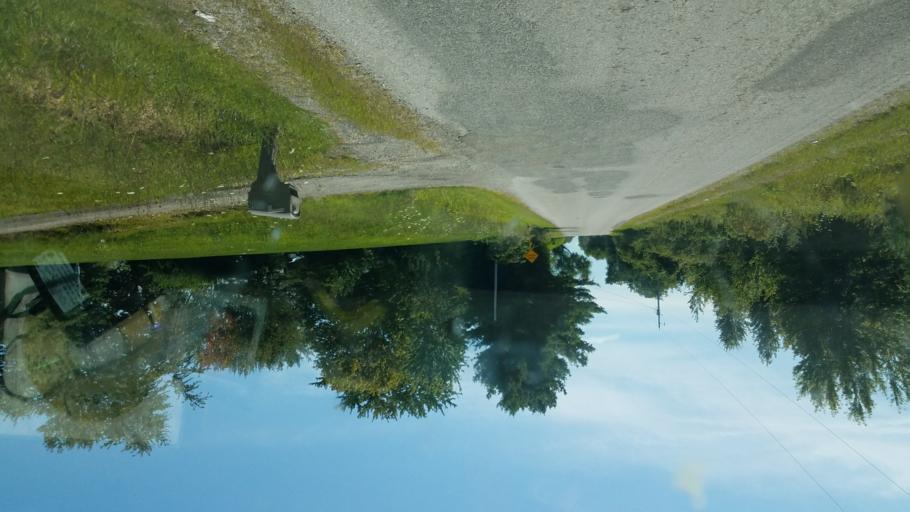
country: US
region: Ohio
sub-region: Knox County
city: Centerburg
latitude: 40.4258
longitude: -82.7383
